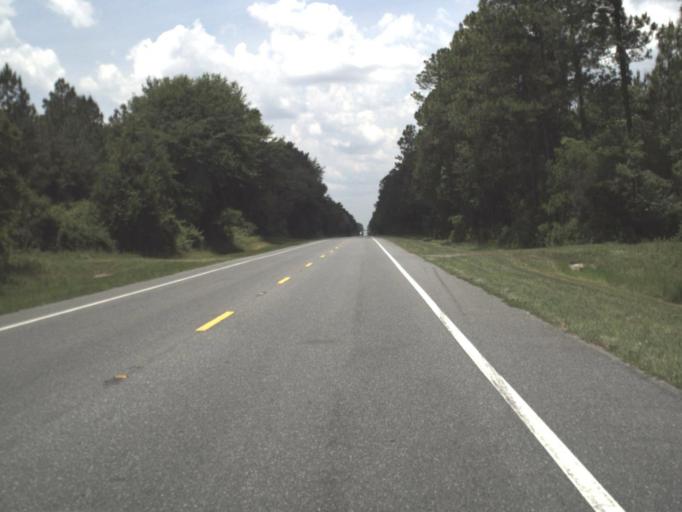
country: US
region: Florida
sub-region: Columbia County
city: Watertown
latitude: 30.1297
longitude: -82.5225
